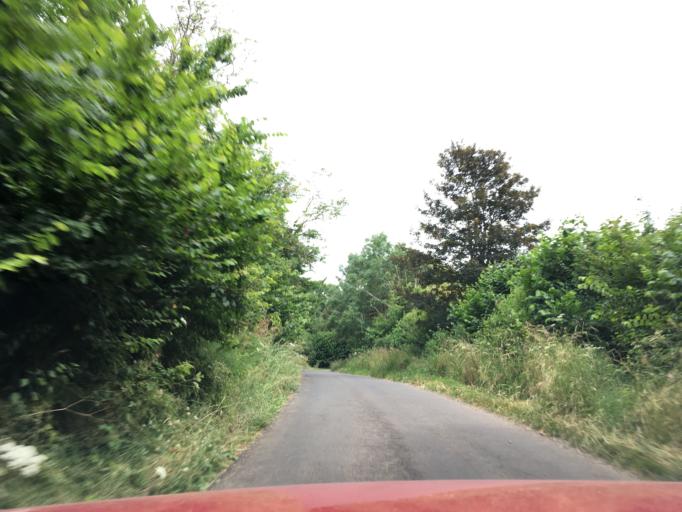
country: GB
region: England
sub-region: Oxfordshire
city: Hook Norton
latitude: 51.9500
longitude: -1.4449
